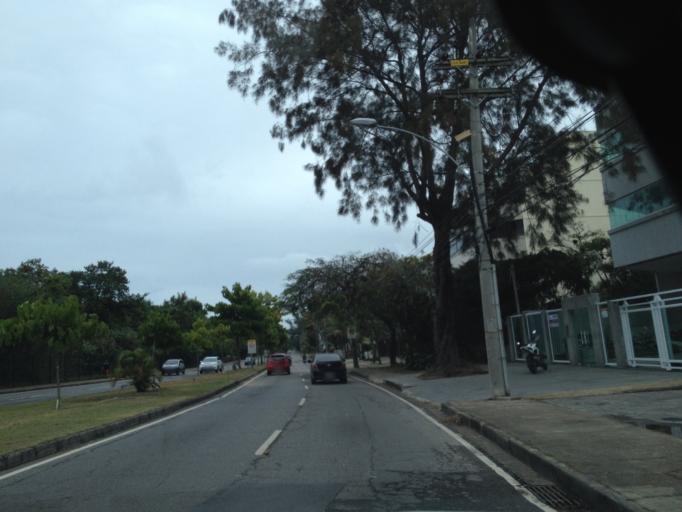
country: BR
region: Rio de Janeiro
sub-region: Nilopolis
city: Nilopolis
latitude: -23.0146
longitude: -43.4467
